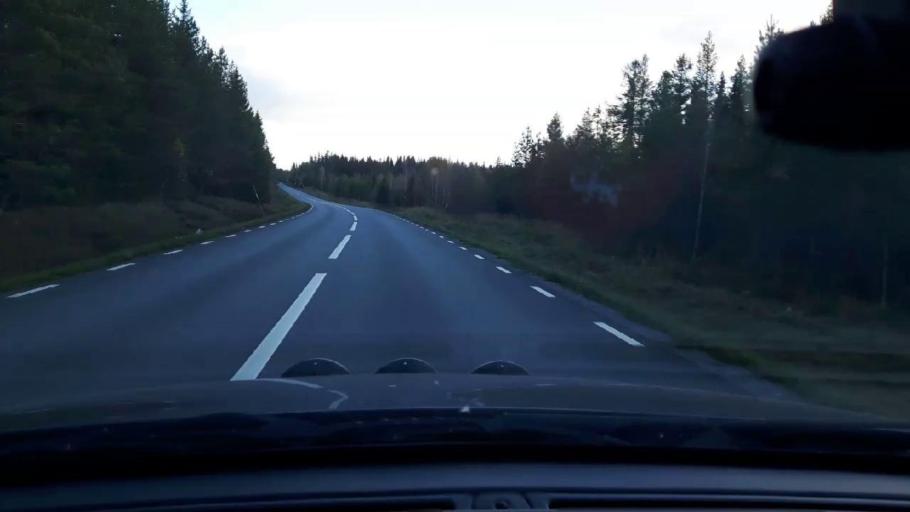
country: SE
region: Jaemtland
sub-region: Bergs Kommun
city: Hoverberg
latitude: 63.0486
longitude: 14.3296
